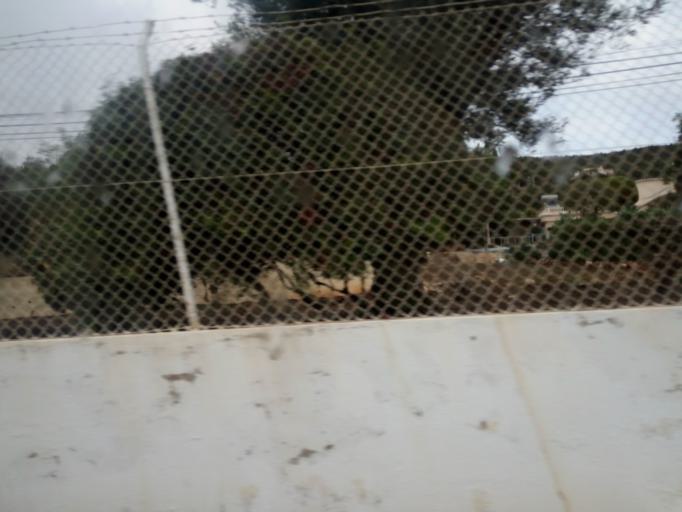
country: PT
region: Faro
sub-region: Faro
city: Santa Barbara de Nexe
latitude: 37.1050
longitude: -7.9846
